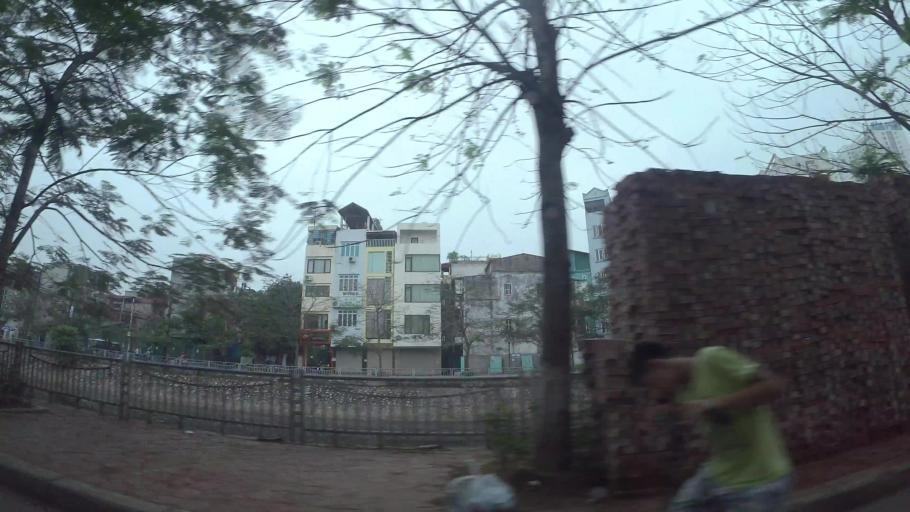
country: VN
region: Ha Noi
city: Hai BaTrung
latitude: 20.9862
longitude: 105.8448
